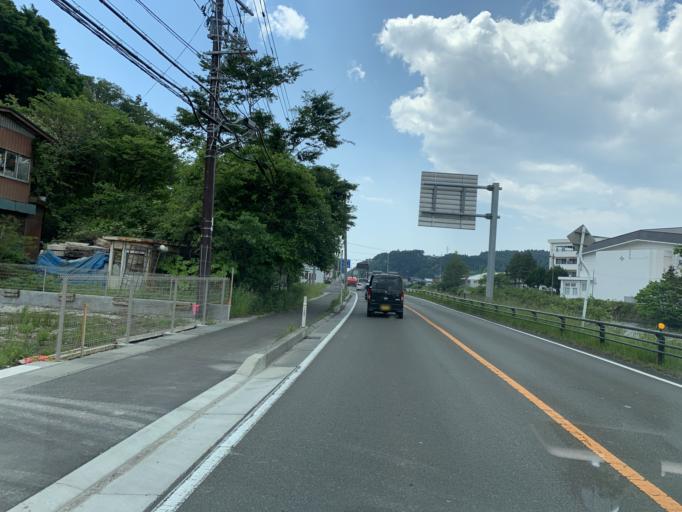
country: JP
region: Miyagi
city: Matsushima
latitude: 38.3977
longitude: 141.0674
